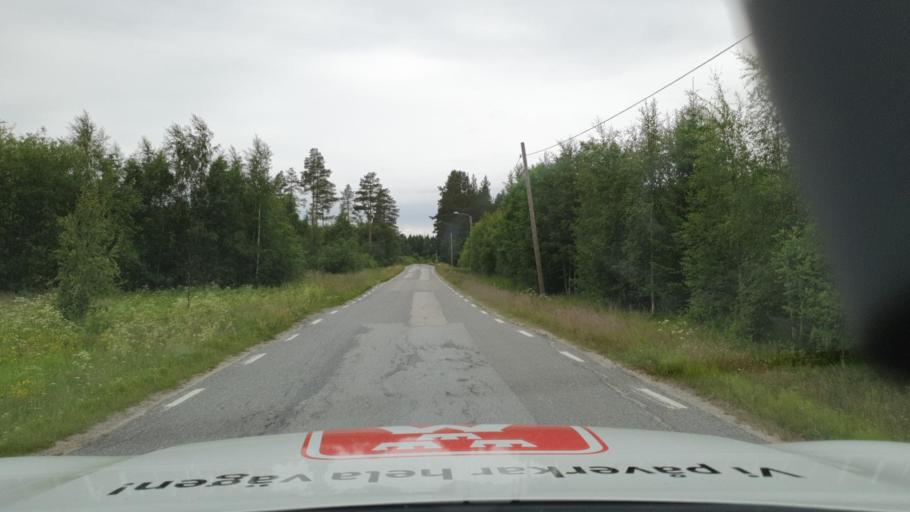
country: SE
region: Vaesterbotten
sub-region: Nordmalings Kommun
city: Nordmaling
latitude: 63.4978
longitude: 19.4278
